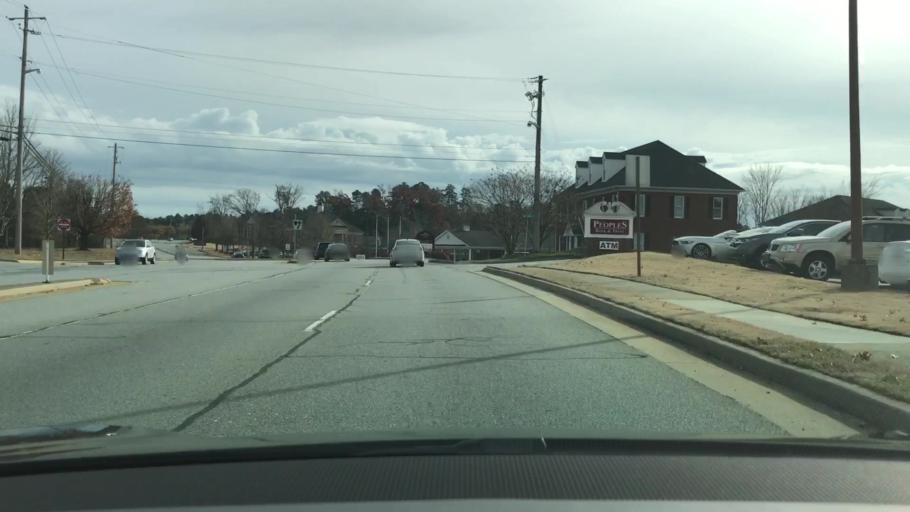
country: US
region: Georgia
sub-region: Gwinnett County
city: Buford
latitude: 34.1047
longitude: -84.0031
